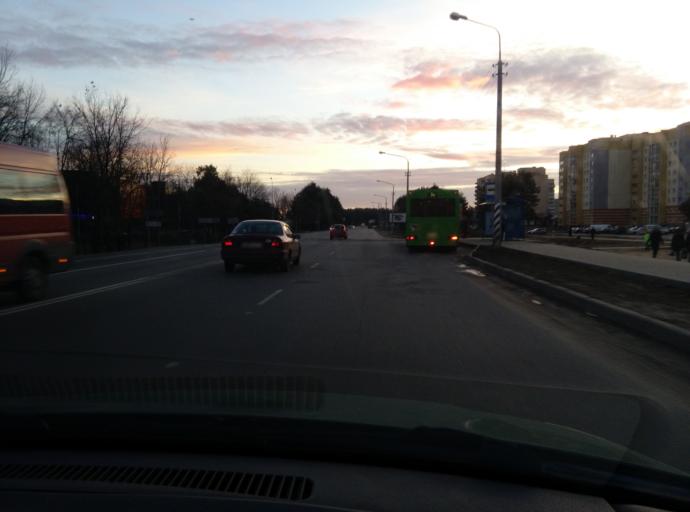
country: BY
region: Minsk
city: Horad Barysaw
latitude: 54.2085
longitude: 28.4854
